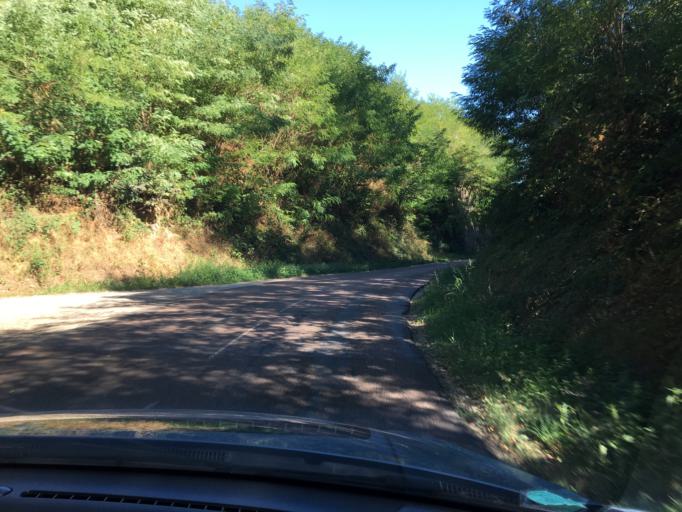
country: FR
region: Bourgogne
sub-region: Departement de l'Yonne
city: Appoigny
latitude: 47.8737
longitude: 3.5091
